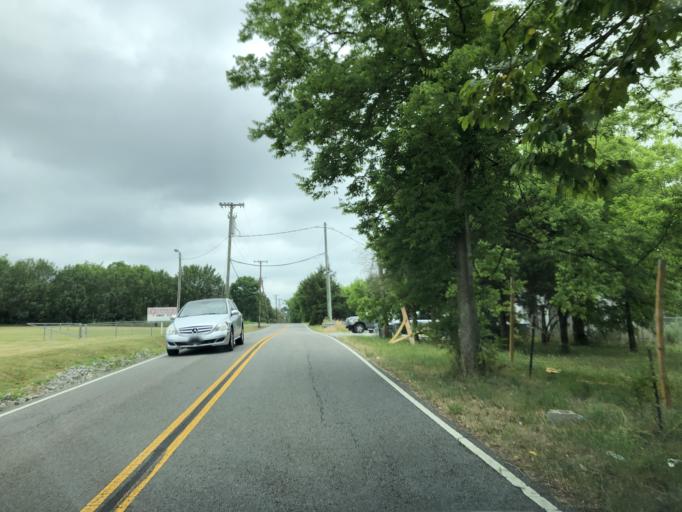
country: US
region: Tennessee
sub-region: Davidson County
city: Goodlettsville
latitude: 36.2885
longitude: -86.7443
